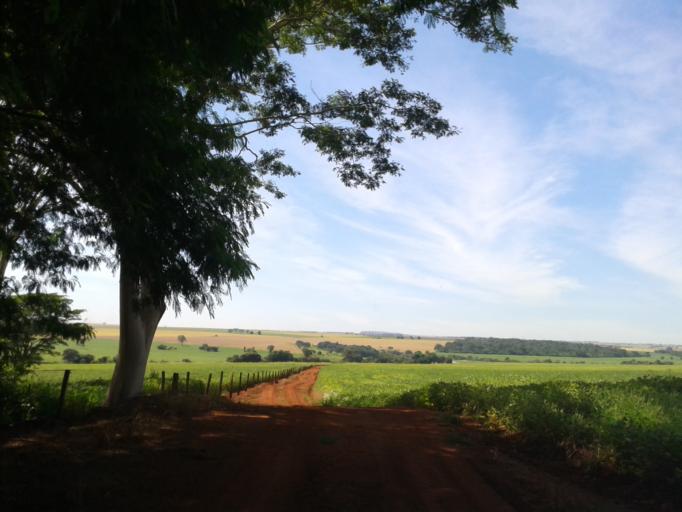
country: BR
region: Minas Gerais
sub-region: Capinopolis
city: Capinopolis
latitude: -18.6431
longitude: -49.7162
